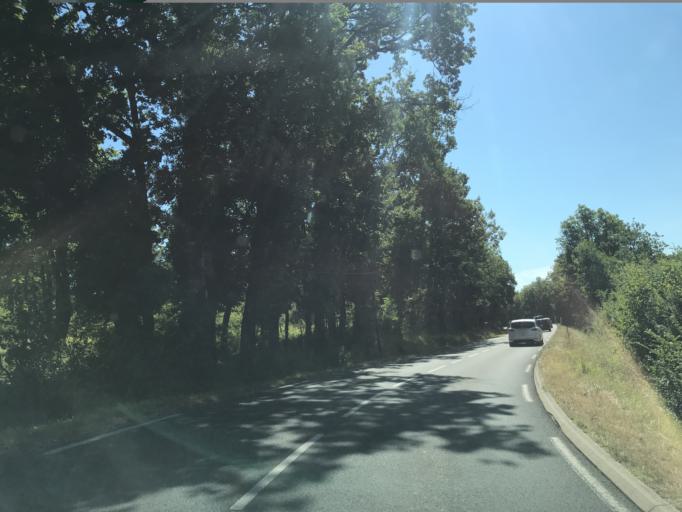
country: FR
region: Limousin
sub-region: Departement de la Correze
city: Larche
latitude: 45.0955
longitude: 1.3889
